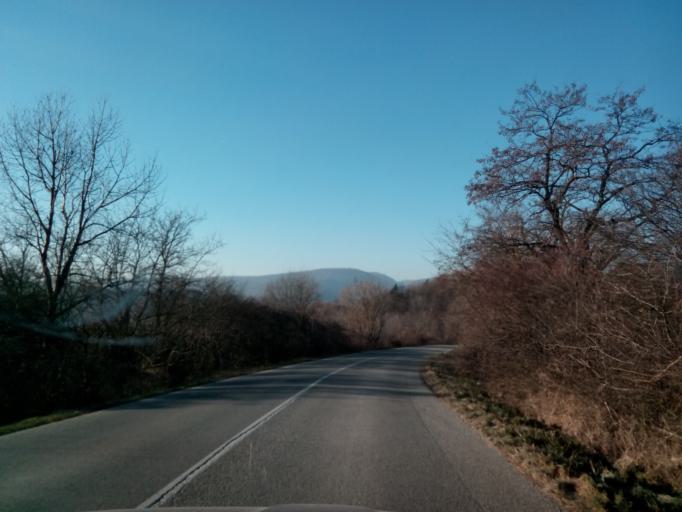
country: SK
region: Kosicky
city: Moldava nad Bodvou
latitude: 48.6843
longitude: 20.9853
